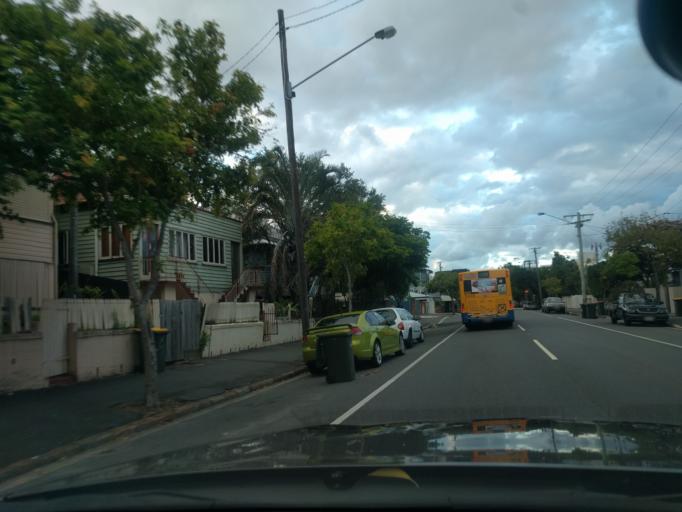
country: AU
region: Queensland
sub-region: Brisbane
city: Balmoral
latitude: -27.4649
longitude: 153.0484
